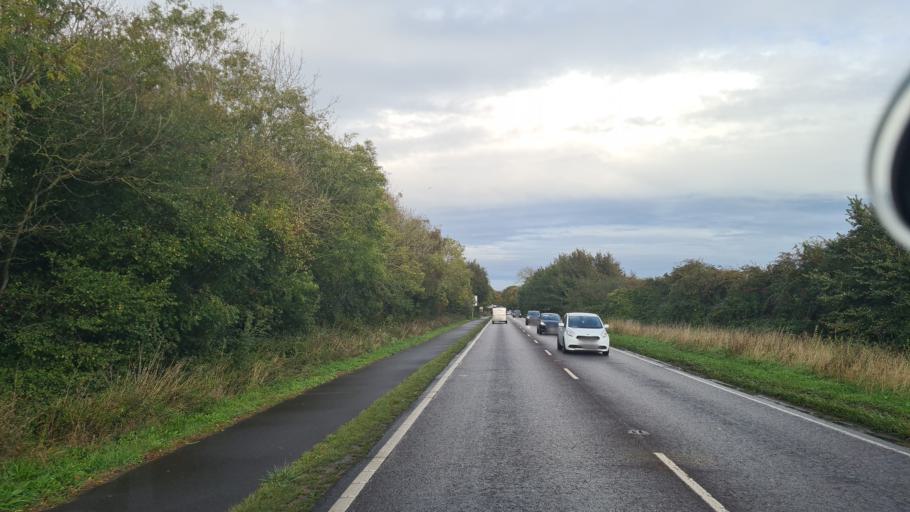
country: GB
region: England
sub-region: West Sussex
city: Littlehampton
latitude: 50.8075
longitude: -0.5807
